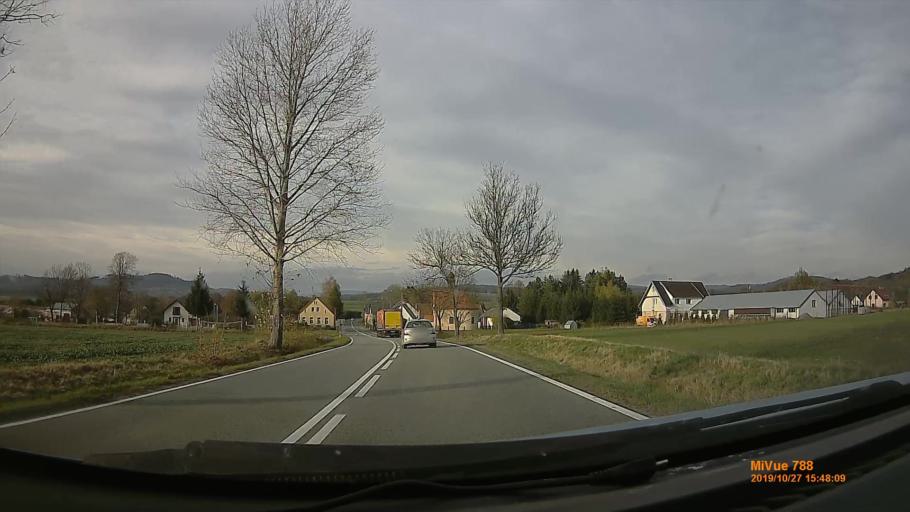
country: PL
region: Lower Silesian Voivodeship
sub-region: Powiat klodzki
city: Bozkow
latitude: 50.4952
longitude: 16.5871
